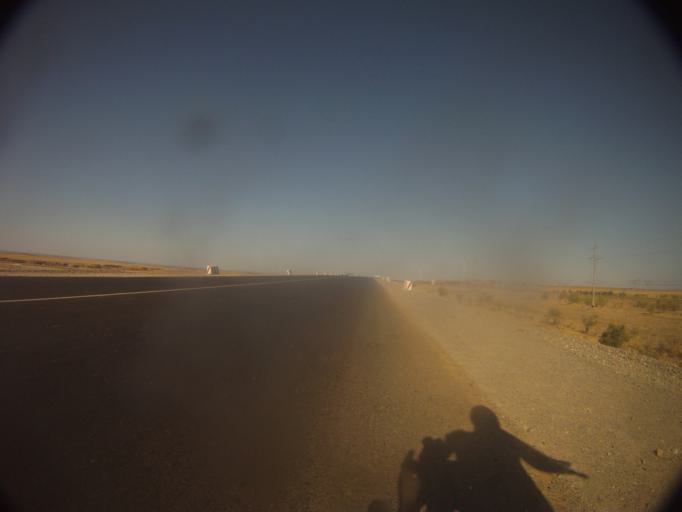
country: KZ
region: Zhambyl
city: Sarykemer
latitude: 42.9811
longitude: 71.5794
